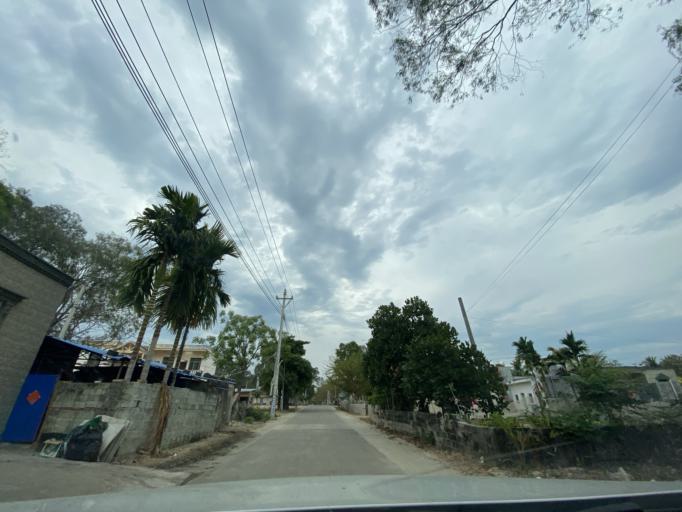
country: CN
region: Hainan
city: Yingzhou
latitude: 18.4194
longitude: 109.8224
